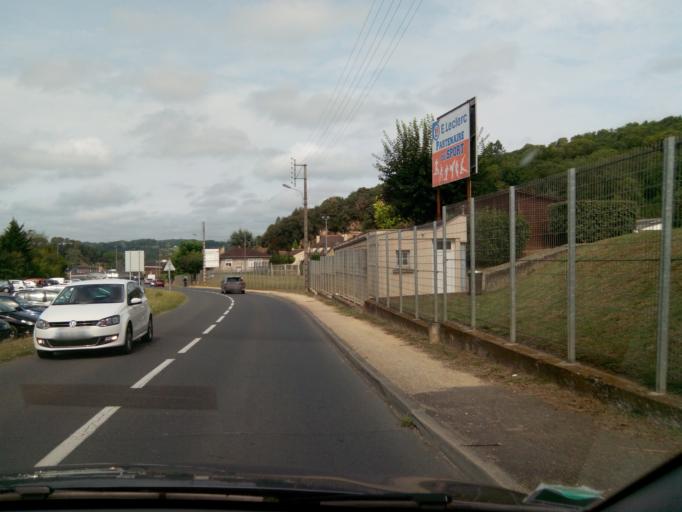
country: FR
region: Aquitaine
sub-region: Departement de la Dordogne
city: Sarlat-la-Caneda
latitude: 44.8751
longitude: 1.2300
